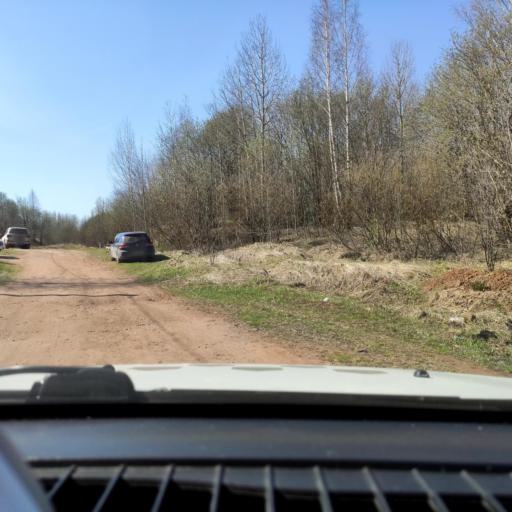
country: RU
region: Perm
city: Perm
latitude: 58.0672
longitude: 56.3751
